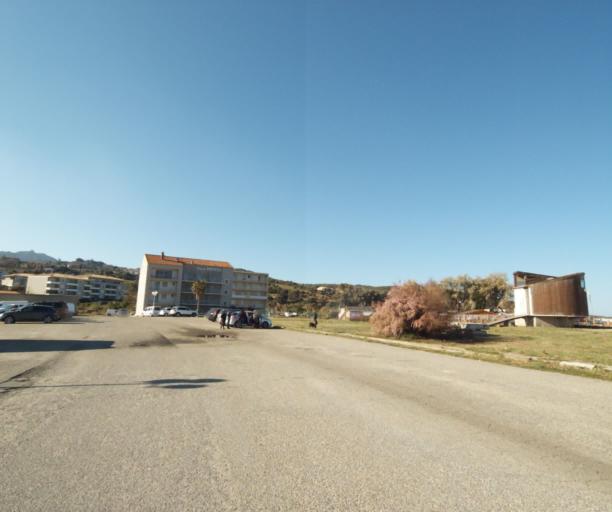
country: FR
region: Corsica
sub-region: Departement de la Corse-du-Sud
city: Propriano
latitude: 41.6762
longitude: 8.8972
